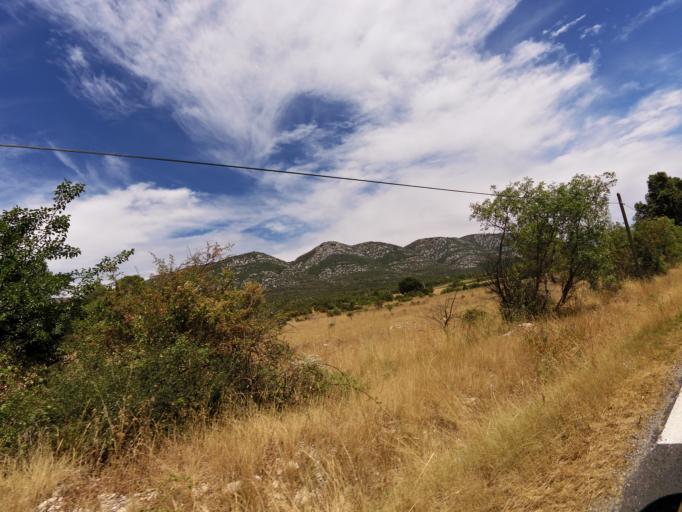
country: FR
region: Languedoc-Roussillon
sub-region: Departement de l'Herault
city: Laroque
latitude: 43.9480
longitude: 3.7653
